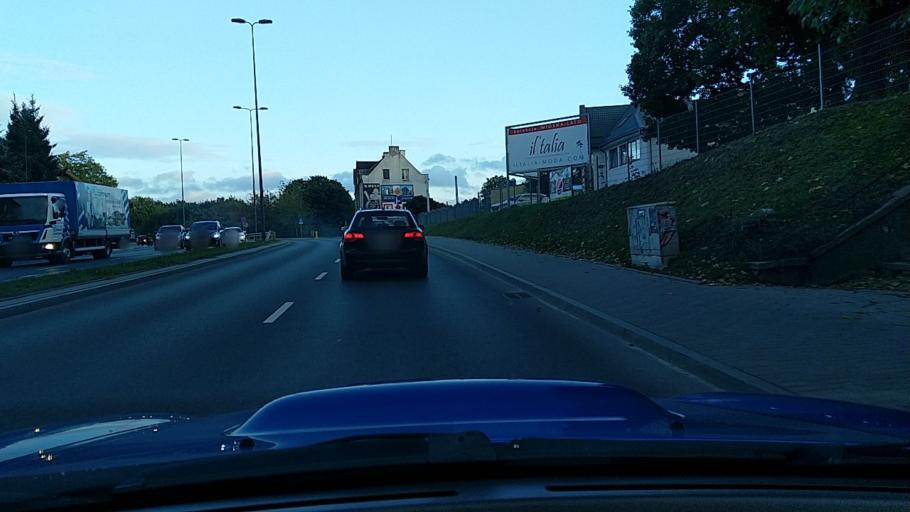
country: PL
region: Warmian-Masurian Voivodeship
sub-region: Powiat olsztynski
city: Olsztyn
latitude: 53.7681
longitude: 20.4827
